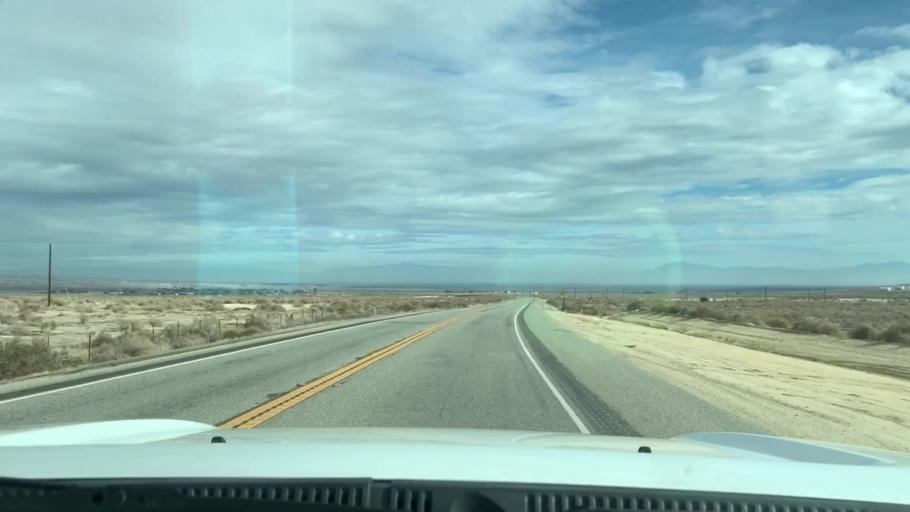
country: US
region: California
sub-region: Kern County
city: Ford City
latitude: 35.1870
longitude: -119.4443
